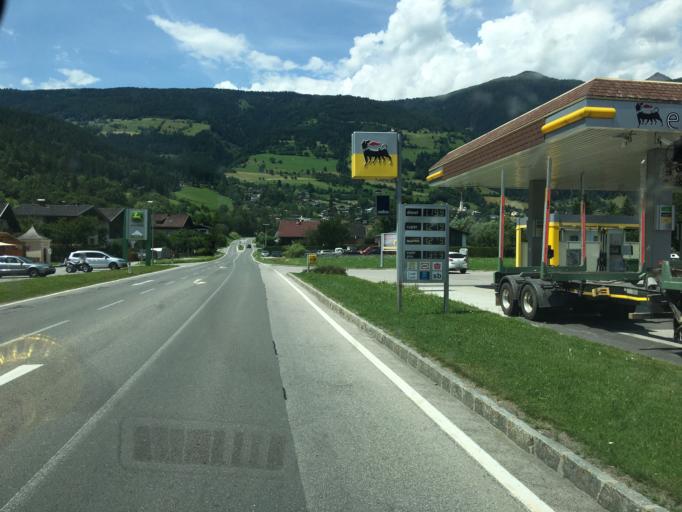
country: AT
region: Carinthia
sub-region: Politischer Bezirk Spittal an der Drau
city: Winklern
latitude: 46.8614
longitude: 12.8922
